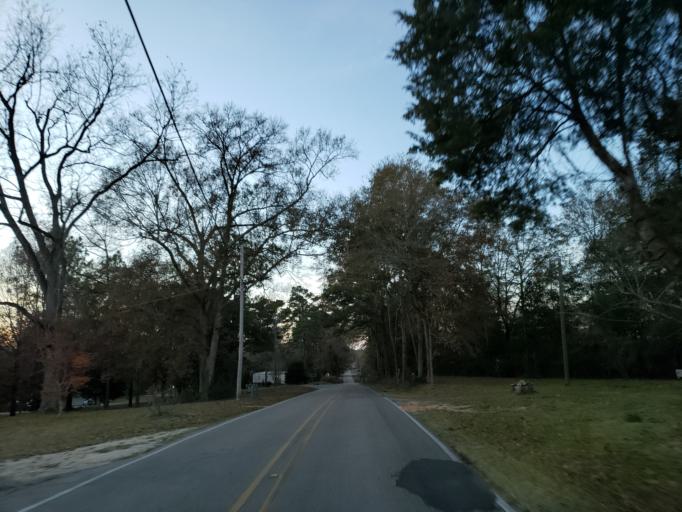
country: US
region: Mississippi
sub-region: Forrest County
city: Hattiesburg
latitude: 31.2441
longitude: -89.3194
